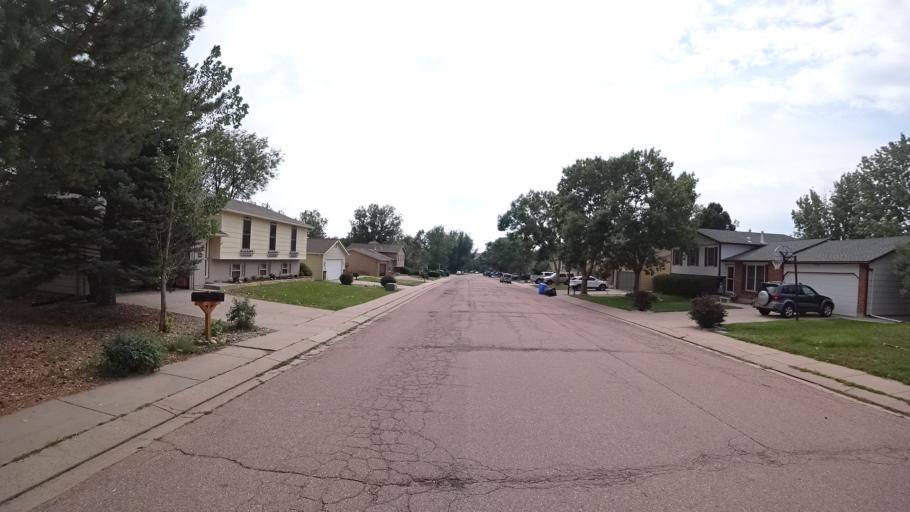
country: US
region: Colorado
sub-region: El Paso County
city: Air Force Academy
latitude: 38.9245
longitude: -104.8332
